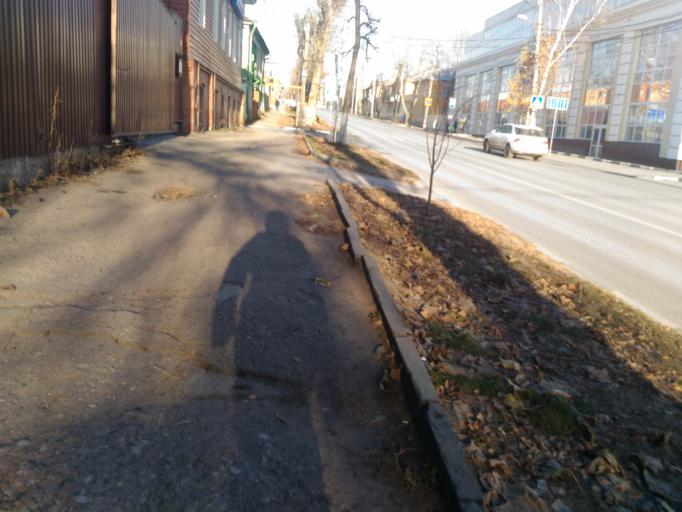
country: RU
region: Ulyanovsk
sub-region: Ulyanovskiy Rayon
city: Ulyanovsk
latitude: 54.3156
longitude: 48.3815
